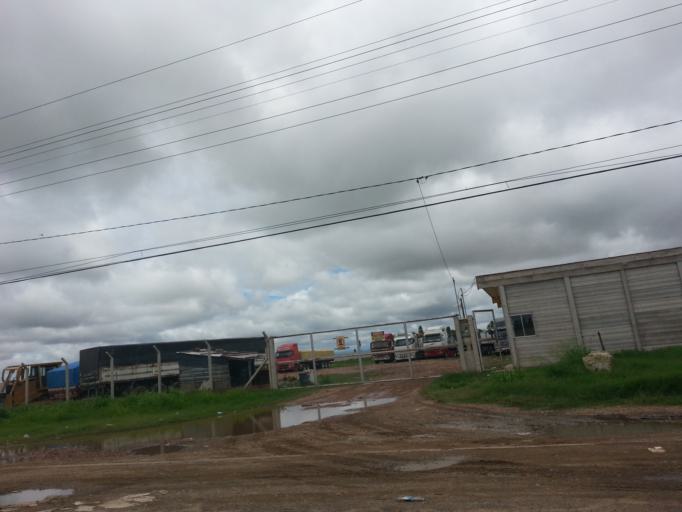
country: BO
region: Santa Cruz
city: La Belgica
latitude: -17.6201
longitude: -63.1591
